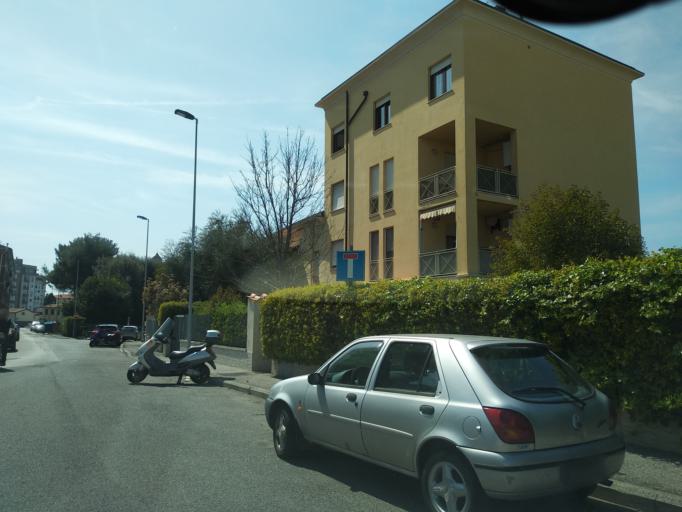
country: IT
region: Tuscany
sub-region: Provincia di Livorno
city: Livorno
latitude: 43.5600
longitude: 10.3205
